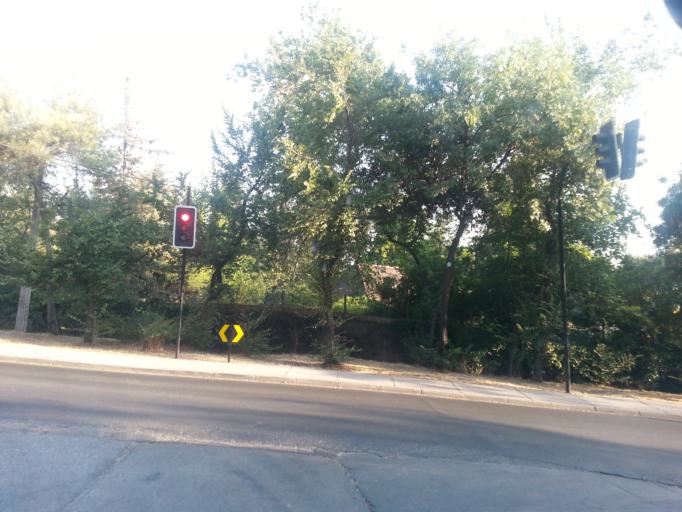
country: CL
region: Santiago Metropolitan
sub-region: Provincia de Santiago
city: Villa Presidente Frei, Nunoa, Santiago, Chile
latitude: -33.3684
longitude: -70.5558
